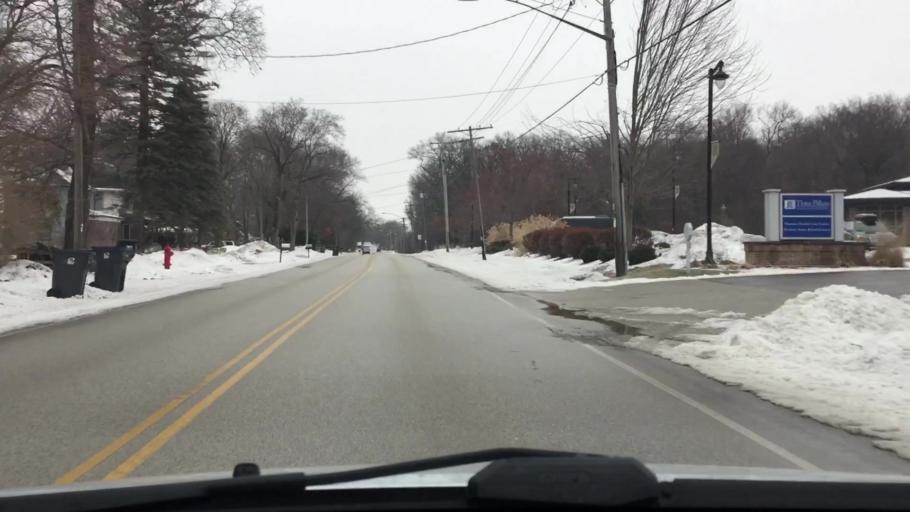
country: US
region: Wisconsin
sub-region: Waukesha County
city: Dousman
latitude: 43.0201
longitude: -88.4725
